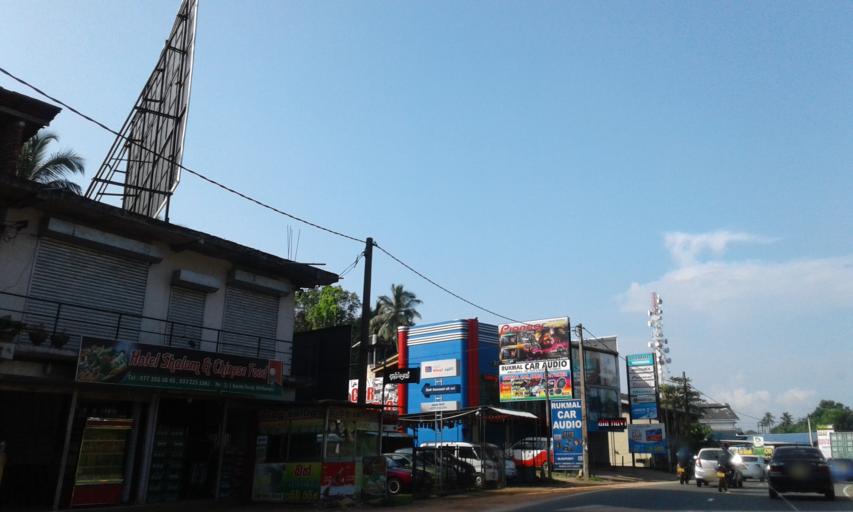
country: LK
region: Western
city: Gampaha
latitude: 7.0221
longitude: 79.9755
